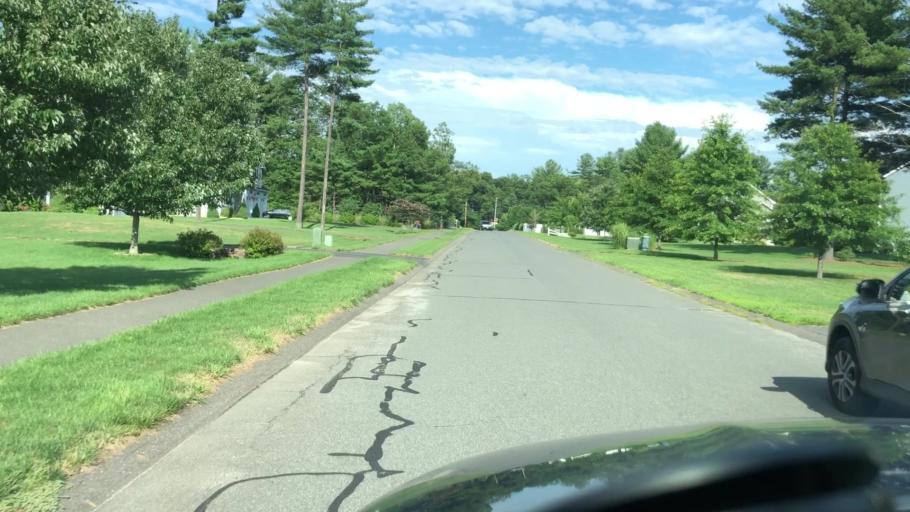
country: US
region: Massachusetts
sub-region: Hampshire County
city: Southampton
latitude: 42.2019
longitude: -72.6923
